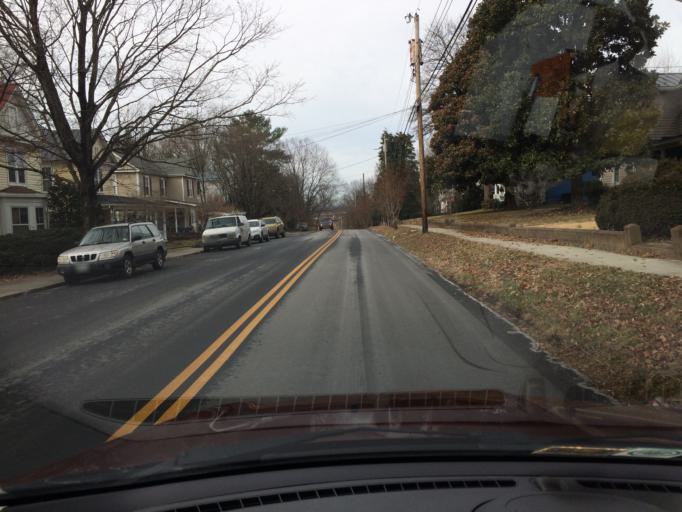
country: US
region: Virginia
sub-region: City of Bedford
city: Bedford
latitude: 37.3372
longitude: -79.5252
